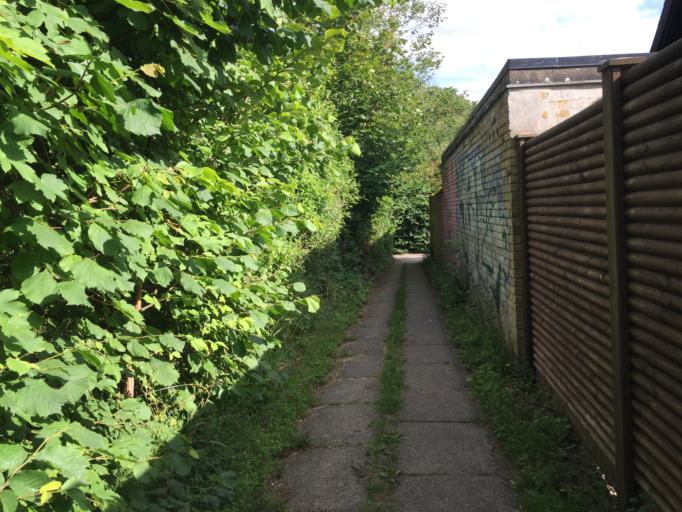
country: DK
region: South Denmark
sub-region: Odense Kommune
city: Odense
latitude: 55.3675
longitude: 10.3795
